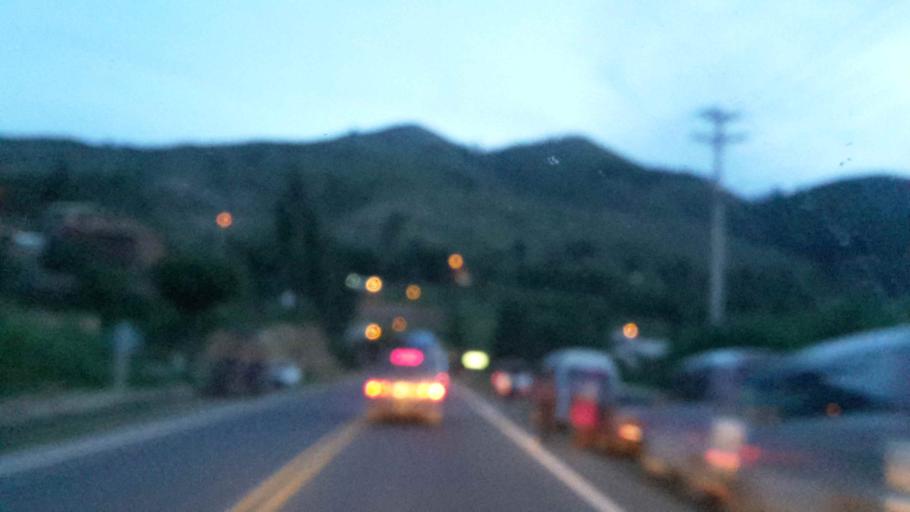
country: BO
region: Cochabamba
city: Colomi
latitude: -17.4164
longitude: -65.9421
